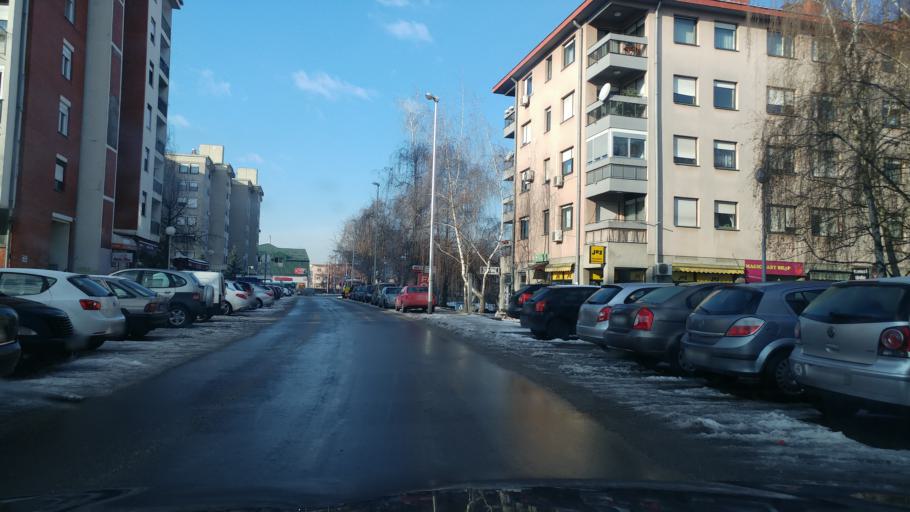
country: HR
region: Grad Zagreb
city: Stenjevec
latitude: 45.8175
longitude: 15.8886
